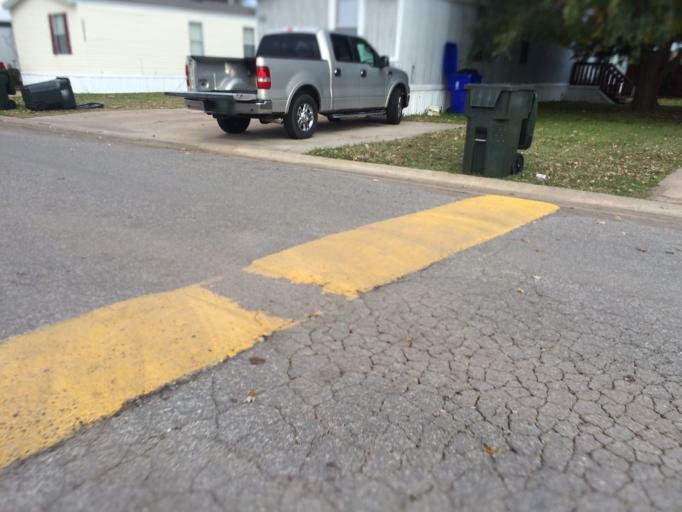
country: US
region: Oklahoma
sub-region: Cleveland County
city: Norman
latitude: 35.2396
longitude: -97.4506
